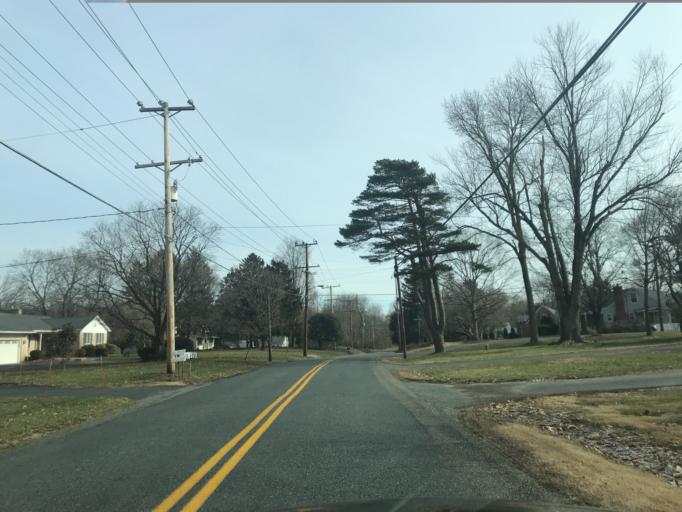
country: US
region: Maryland
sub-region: Harford County
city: Aberdeen
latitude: 39.5735
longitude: -76.1568
